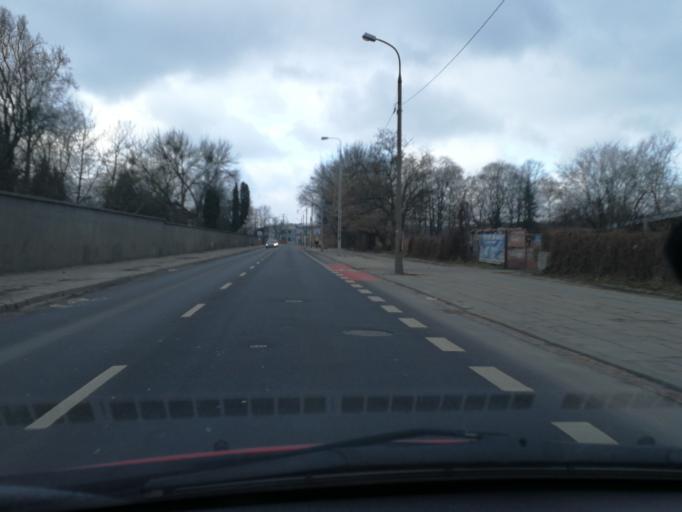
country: PL
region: Masovian Voivodeship
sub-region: Warszawa
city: Zoliborz
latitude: 52.2534
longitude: 20.9677
